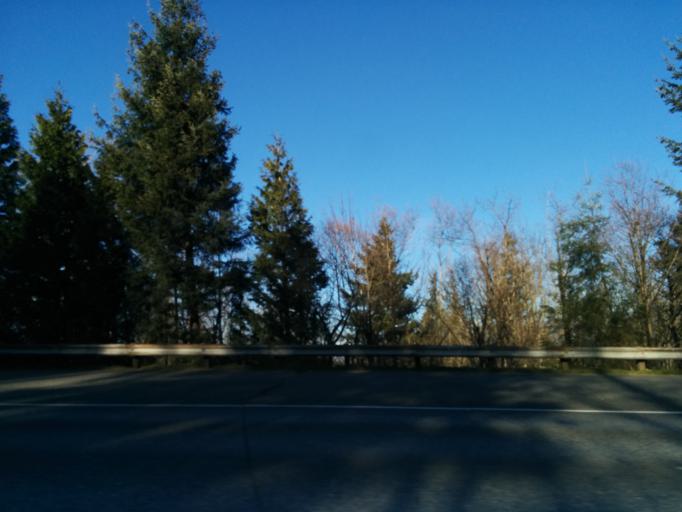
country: US
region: Washington
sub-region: King County
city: Snoqualmie
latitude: 47.5132
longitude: -121.8333
